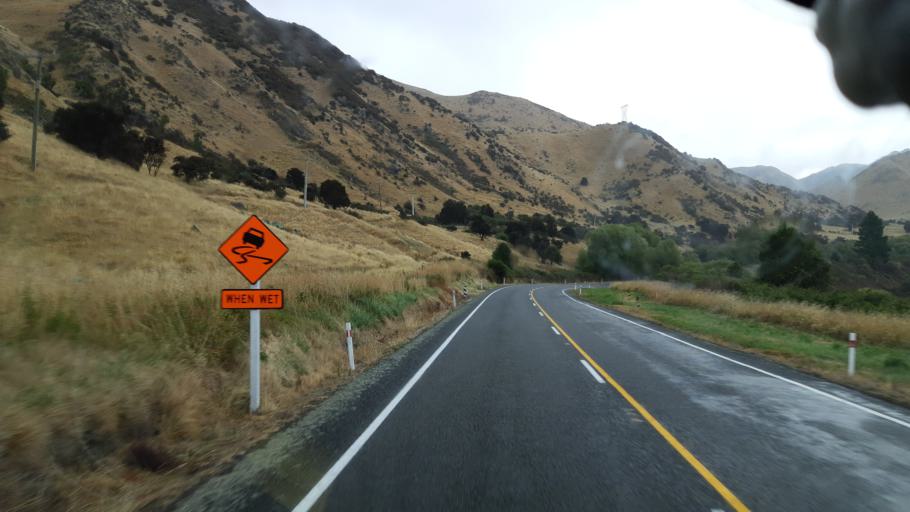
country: NZ
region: Canterbury
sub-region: Hurunui District
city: Amberley
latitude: -42.6704
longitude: 172.7695
